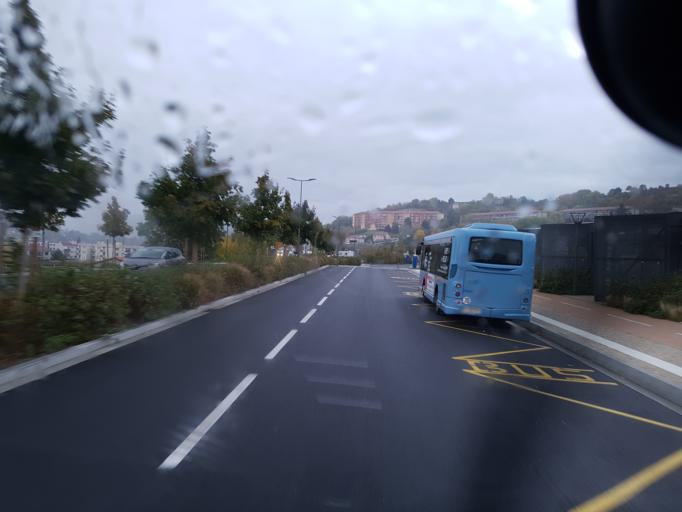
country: FR
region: Auvergne
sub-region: Departement de la Haute-Loire
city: Le Puy-en-Velay
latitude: 45.0440
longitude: 3.8937
